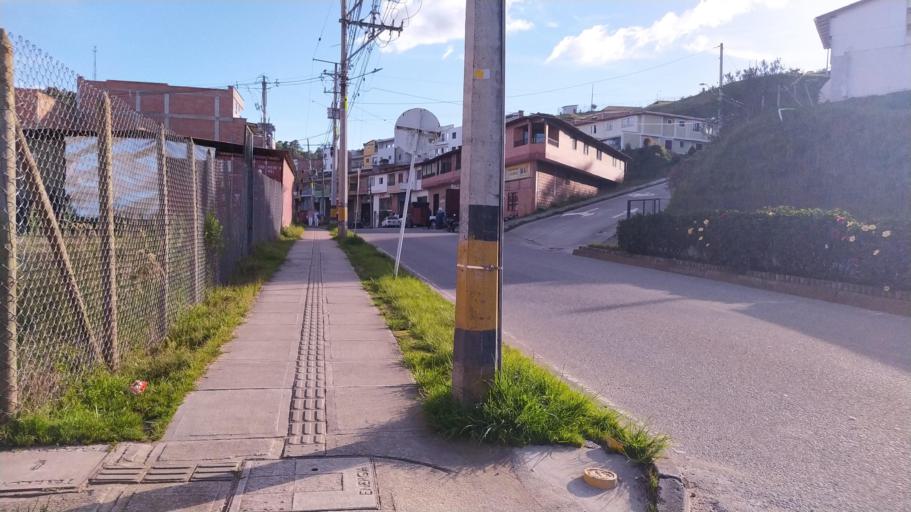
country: CO
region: Antioquia
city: Entrerrios
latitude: 6.5684
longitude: -75.5190
